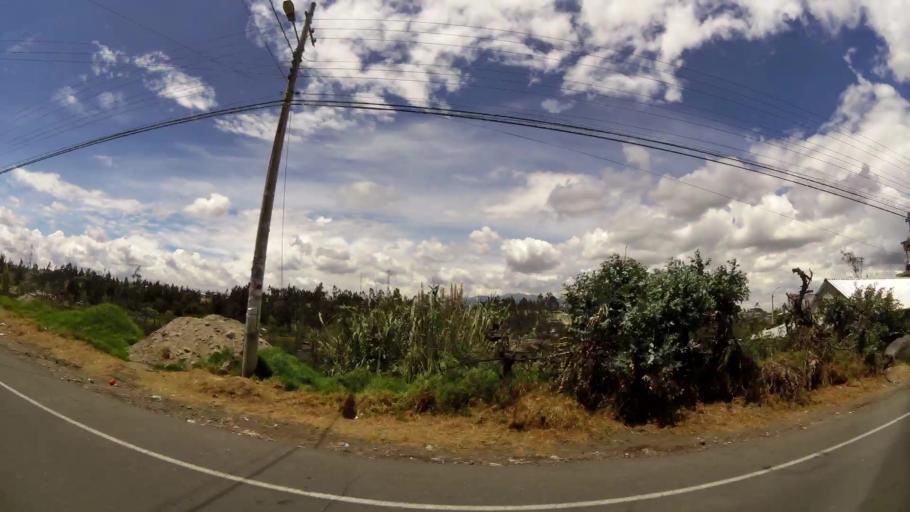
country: EC
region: Tungurahua
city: Ambato
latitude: -1.2809
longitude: -78.5921
